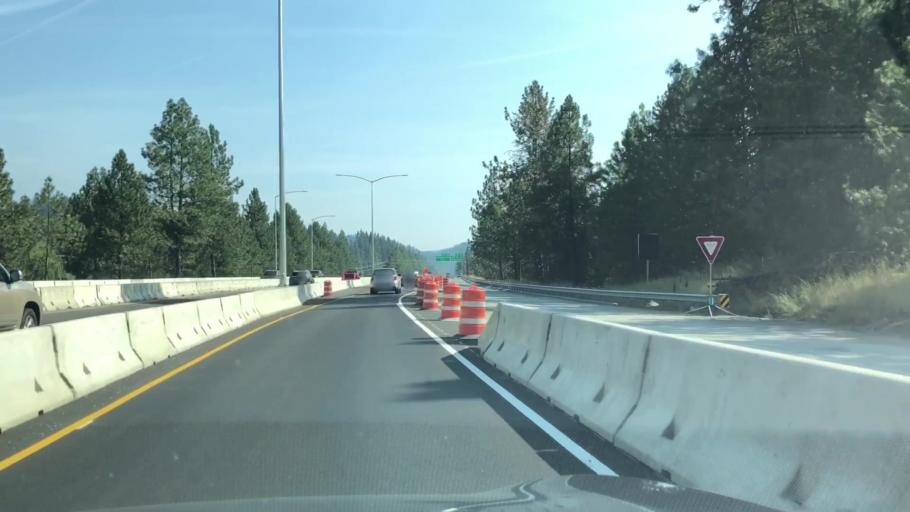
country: US
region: Idaho
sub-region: Kootenai County
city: Coeur d'Alene
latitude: 47.6936
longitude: -116.7698
